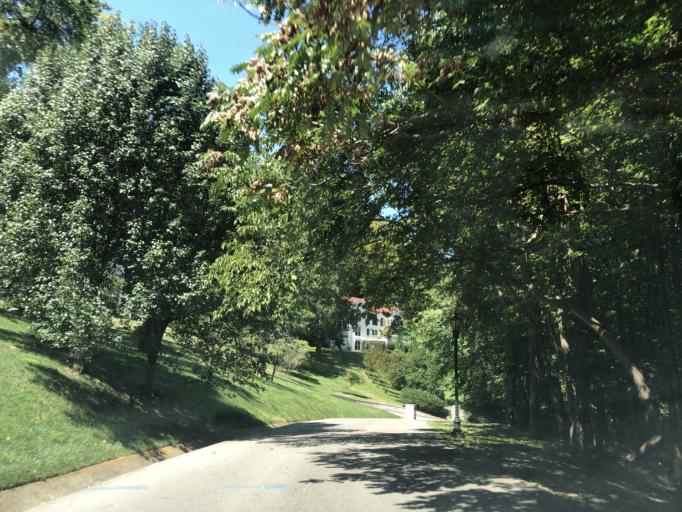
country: US
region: Tennessee
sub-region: Davidson County
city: Oak Hill
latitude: 36.0701
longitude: -86.7833
